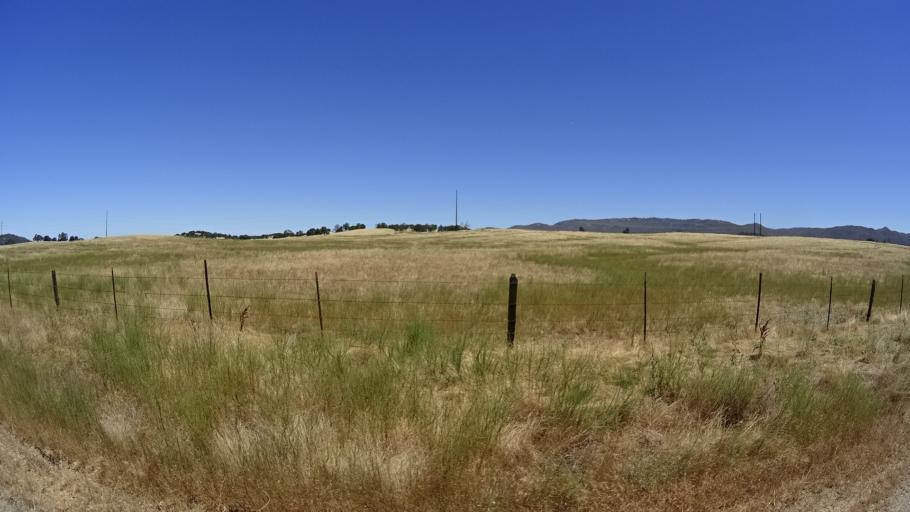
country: US
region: California
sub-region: Calaveras County
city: Rancho Calaveras
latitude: 38.0573
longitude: -120.7641
